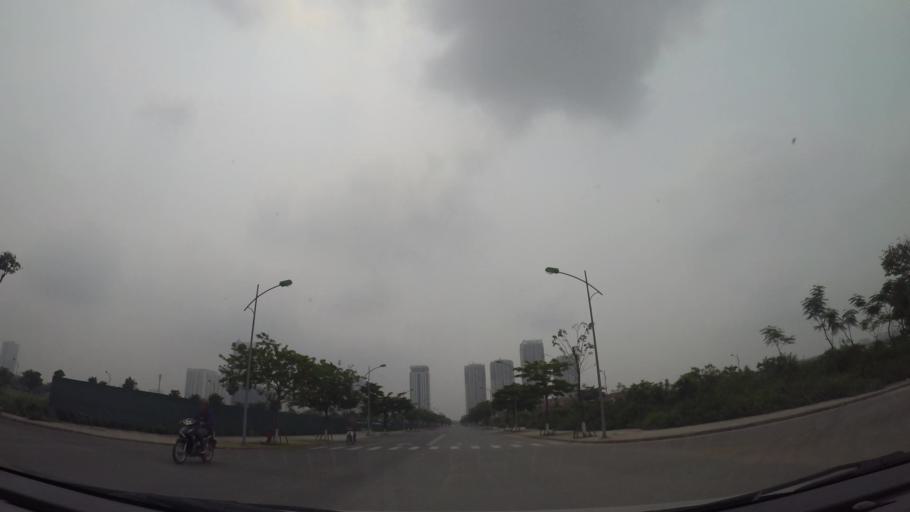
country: VN
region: Ha Noi
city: Ha Dong
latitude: 20.9791
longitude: 105.7534
